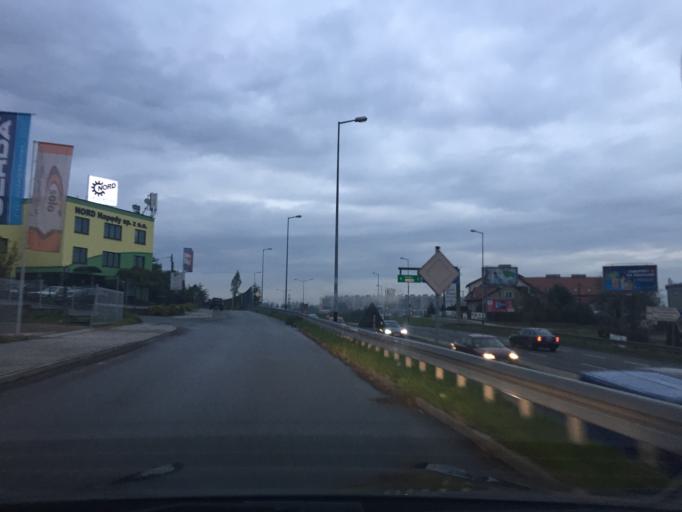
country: PL
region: Lesser Poland Voivodeship
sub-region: Powiat wielicki
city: Wieliczka
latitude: 50.0023
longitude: 20.0248
